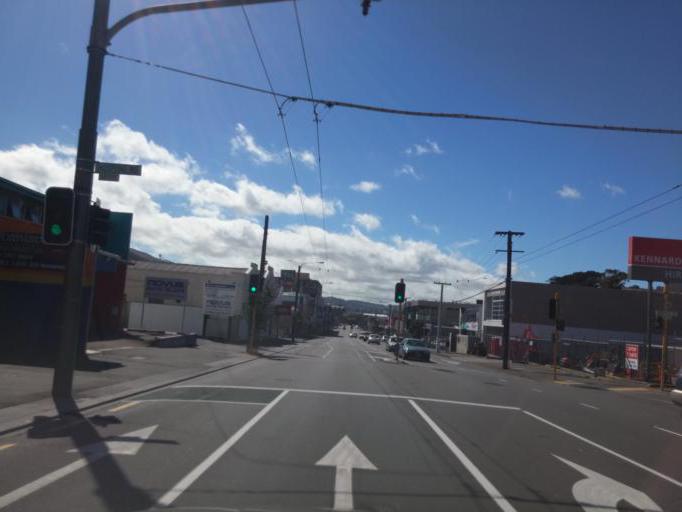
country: NZ
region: Wellington
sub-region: Wellington City
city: Wellington
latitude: -41.3064
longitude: 174.7781
